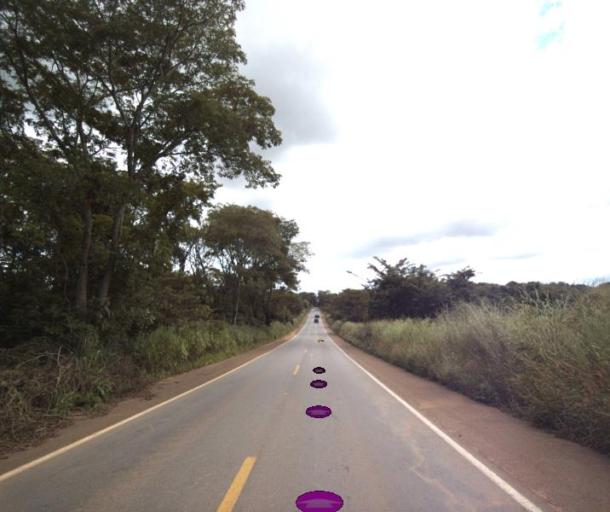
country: BR
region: Goias
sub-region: Pirenopolis
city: Pirenopolis
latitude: -16.0803
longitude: -49.0471
